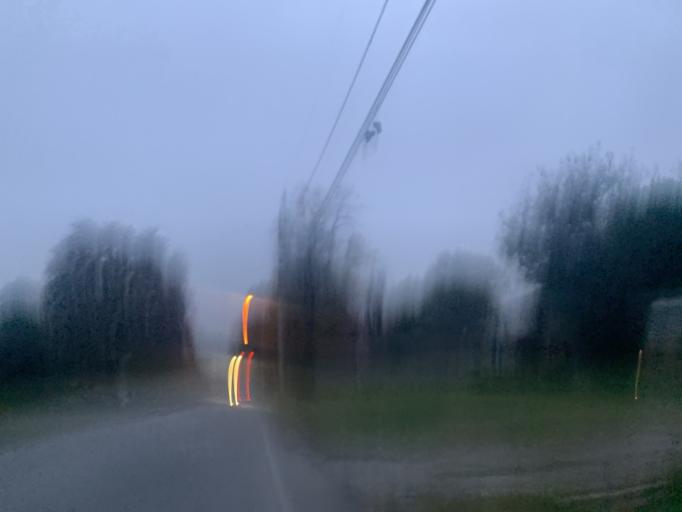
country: US
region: Kentucky
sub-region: Jefferson County
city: Shively
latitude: 38.2162
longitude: -85.7917
